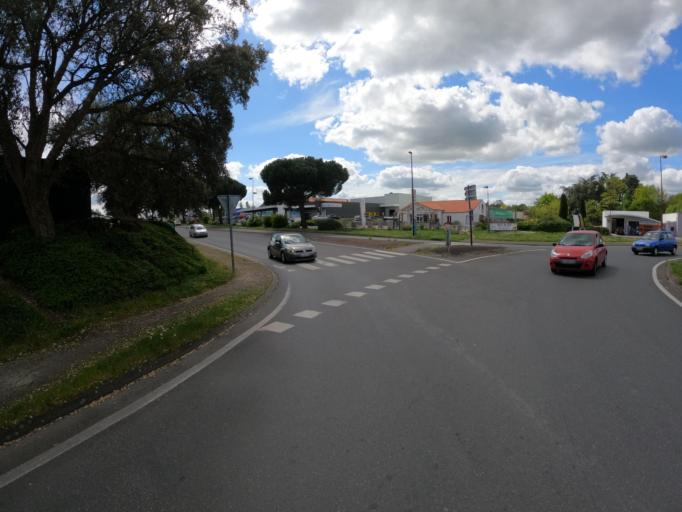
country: FR
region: Pays de la Loire
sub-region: Departement de la Loire-Atlantique
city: Clisson
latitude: 47.0978
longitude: -1.2827
